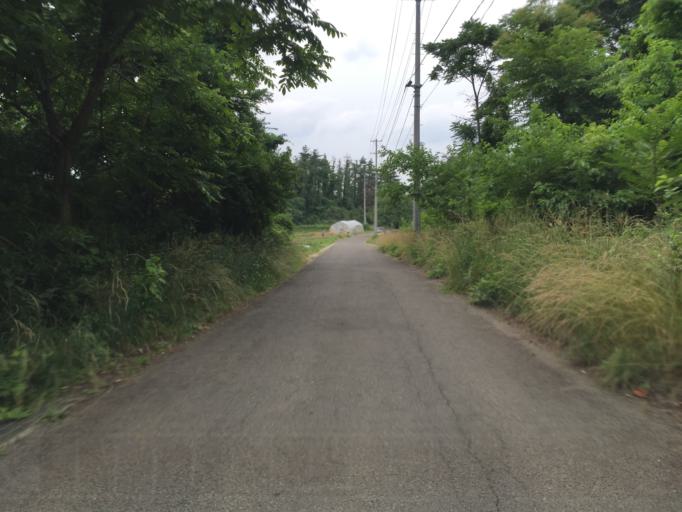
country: JP
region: Fukushima
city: Fukushima-shi
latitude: 37.7131
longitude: 140.4641
